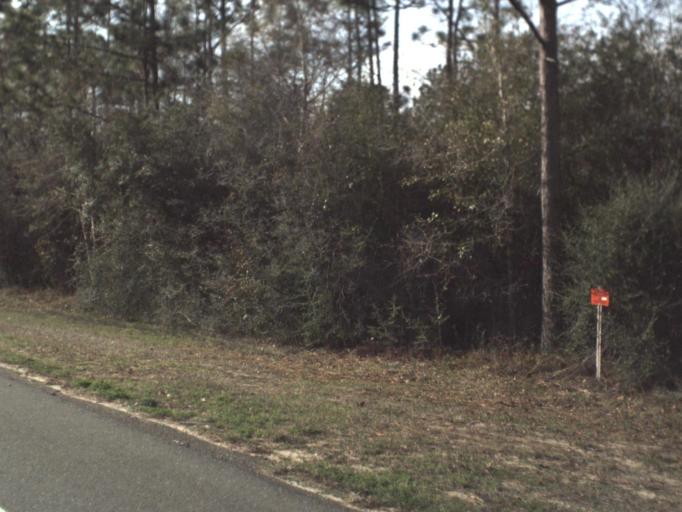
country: US
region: Florida
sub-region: Bay County
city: Youngstown
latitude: 30.4353
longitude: -85.3995
